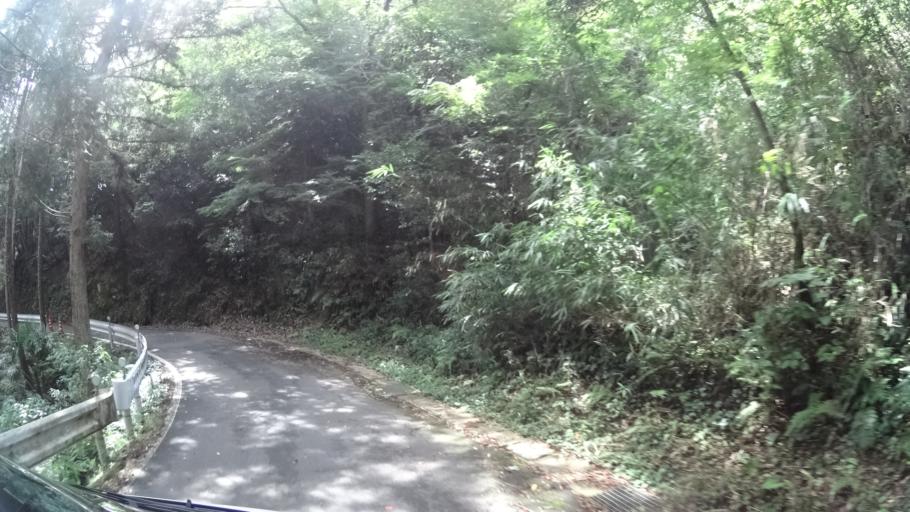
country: JP
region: Kyoto
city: Fukuchiyama
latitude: 35.3678
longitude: 135.1733
